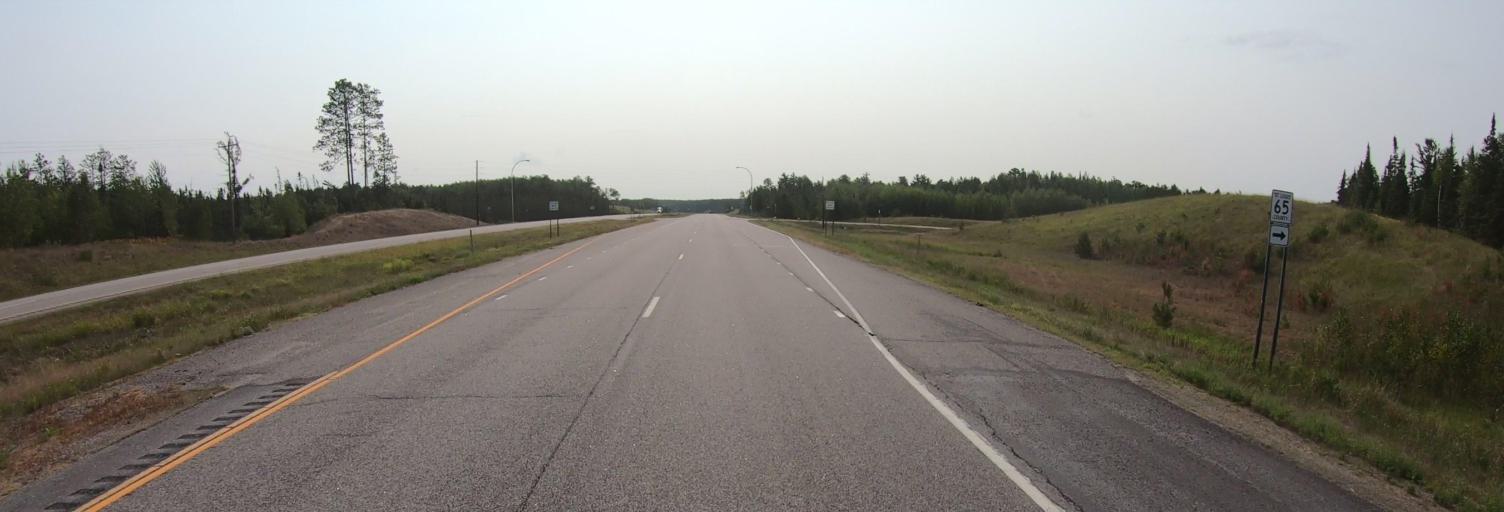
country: US
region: Minnesota
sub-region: Saint Louis County
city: Mountain Iron
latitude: 47.6651
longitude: -92.6369
